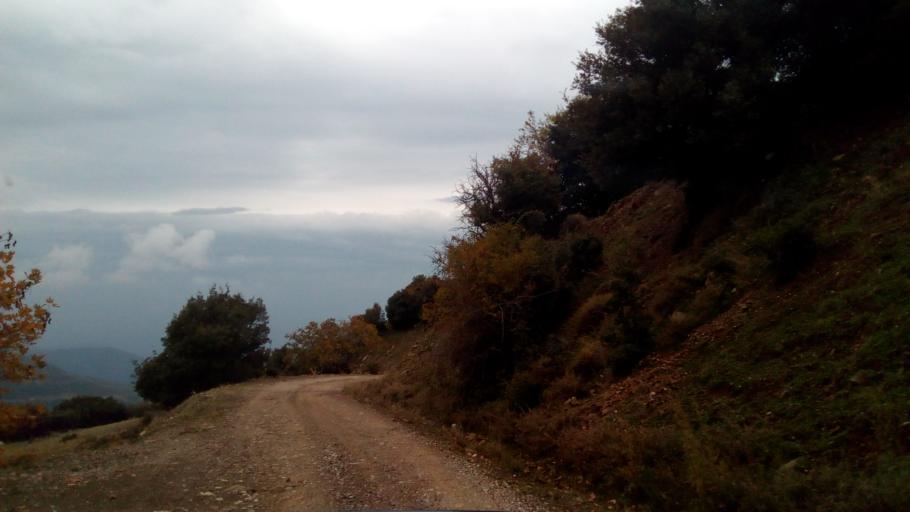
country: GR
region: West Greece
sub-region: Nomos Achaias
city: Selianitika
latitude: 38.4135
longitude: 22.0890
